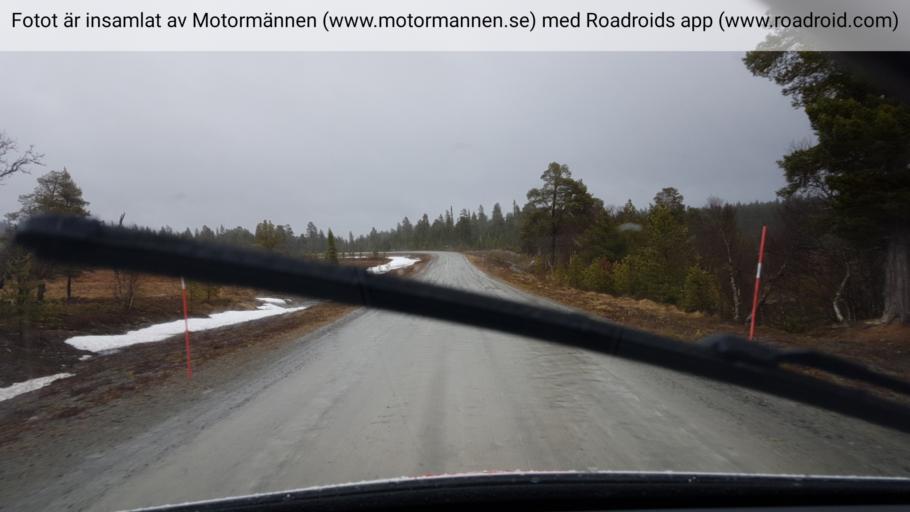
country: SE
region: Jaemtland
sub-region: Are Kommun
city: Are
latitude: 62.6574
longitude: 12.9862
